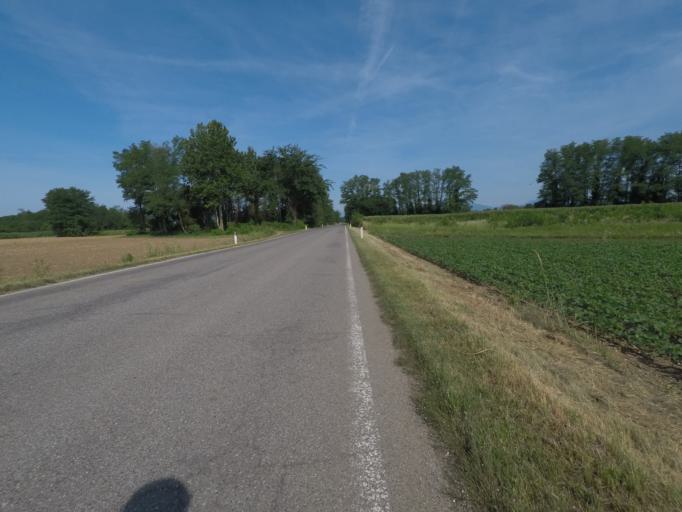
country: IT
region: Friuli Venezia Giulia
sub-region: Provincia di Udine
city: Colloredo di Prato
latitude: 46.0535
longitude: 13.1247
